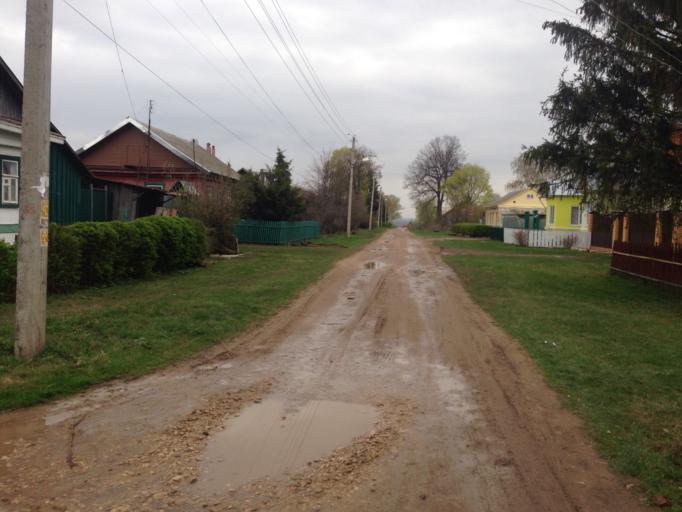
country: RU
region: Tula
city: Krapivna
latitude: 53.9386
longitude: 37.1490
